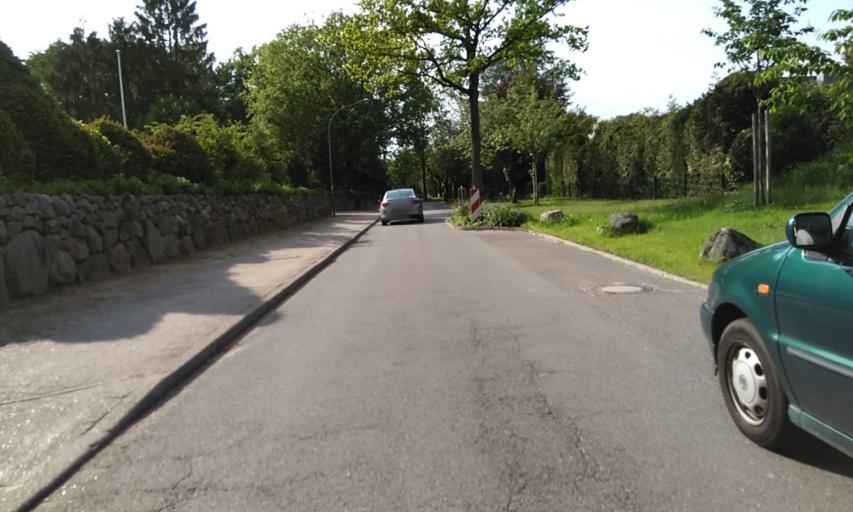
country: DE
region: Lower Saxony
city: Buxtehude
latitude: 53.4581
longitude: 9.7055
